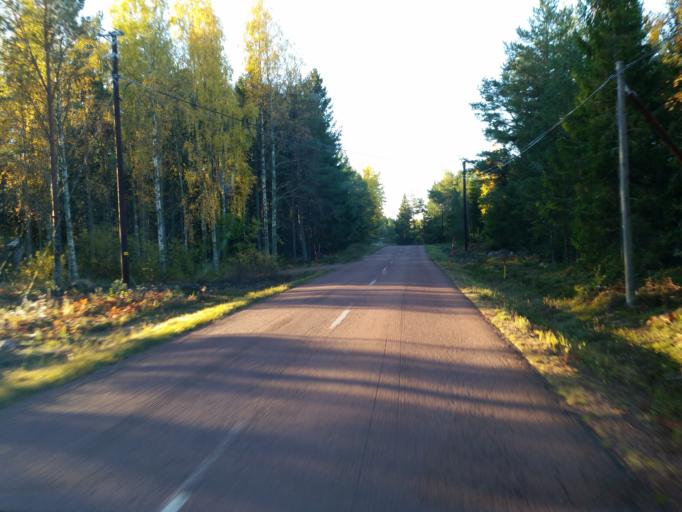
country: AX
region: Alands skaergard
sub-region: Vardoe
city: Vardoe
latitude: 60.3010
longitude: 20.3827
